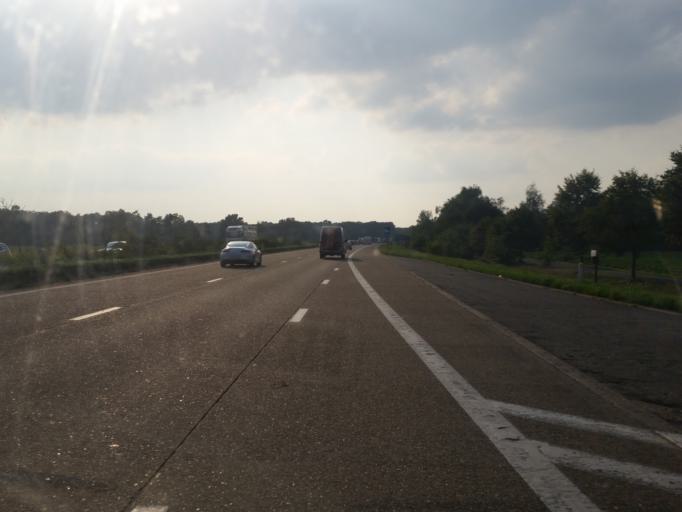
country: BE
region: Flanders
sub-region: Provincie Antwerpen
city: Oud-Turnhout
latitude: 51.2940
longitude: 5.0261
